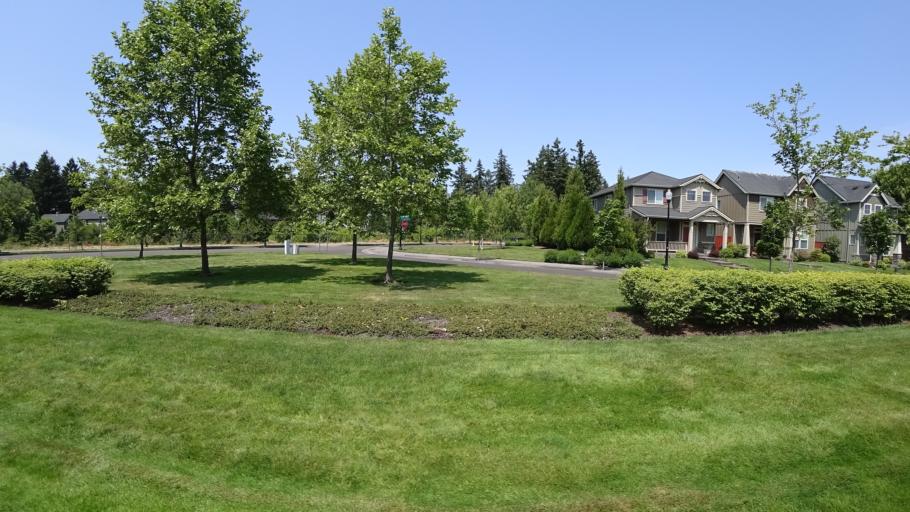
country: US
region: Oregon
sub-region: Washington County
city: Hillsboro
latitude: 45.4960
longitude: -122.9359
